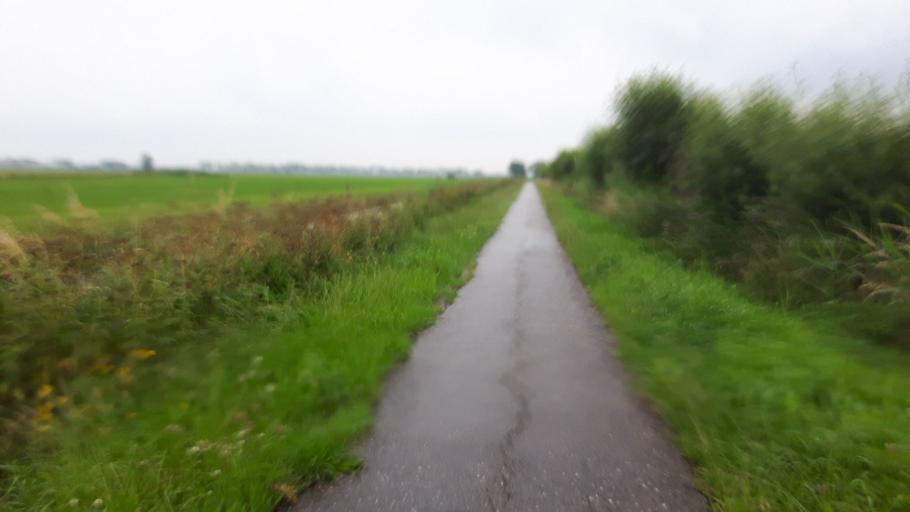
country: NL
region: Utrecht
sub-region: Gemeente Montfoort
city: Montfoort
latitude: 52.0504
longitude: 4.9891
